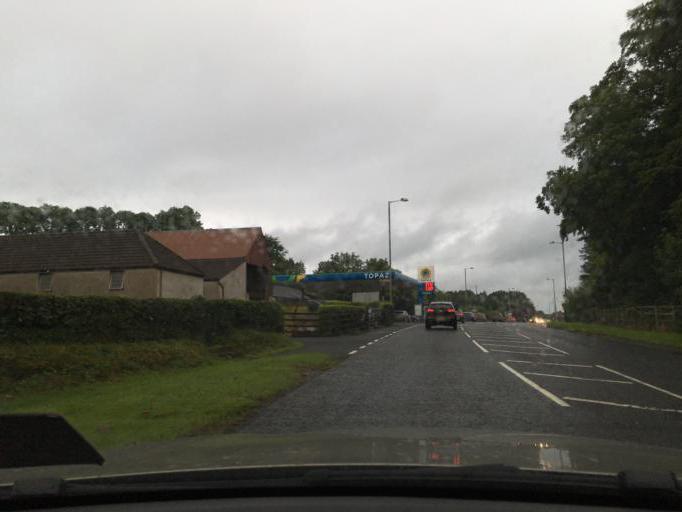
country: GB
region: Northern Ireland
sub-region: Fermanagh District
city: Enniskillen
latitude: 54.3851
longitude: -7.6385
